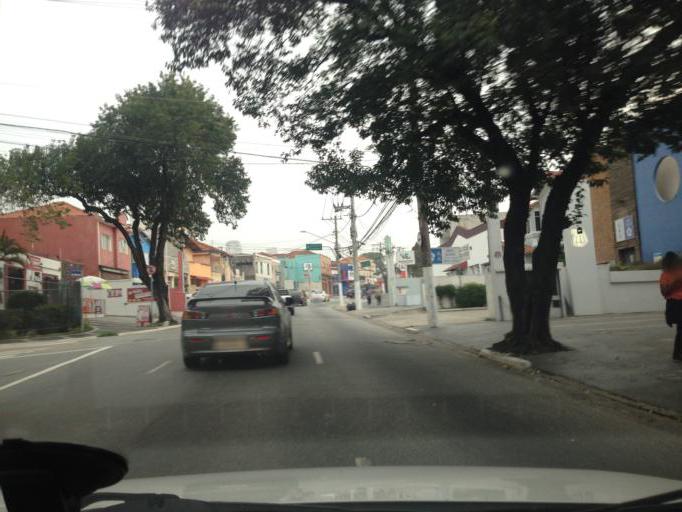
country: BR
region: Sao Paulo
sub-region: Sao Paulo
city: Sao Paulo
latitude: -23.5259
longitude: -46.7072
